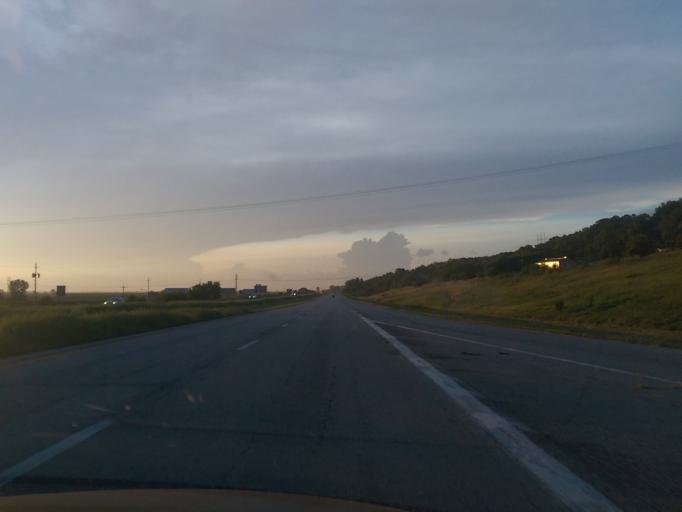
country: US
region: Missouri
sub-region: Atchison County
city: Rock Port
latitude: 40.4112
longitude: -95.5574
